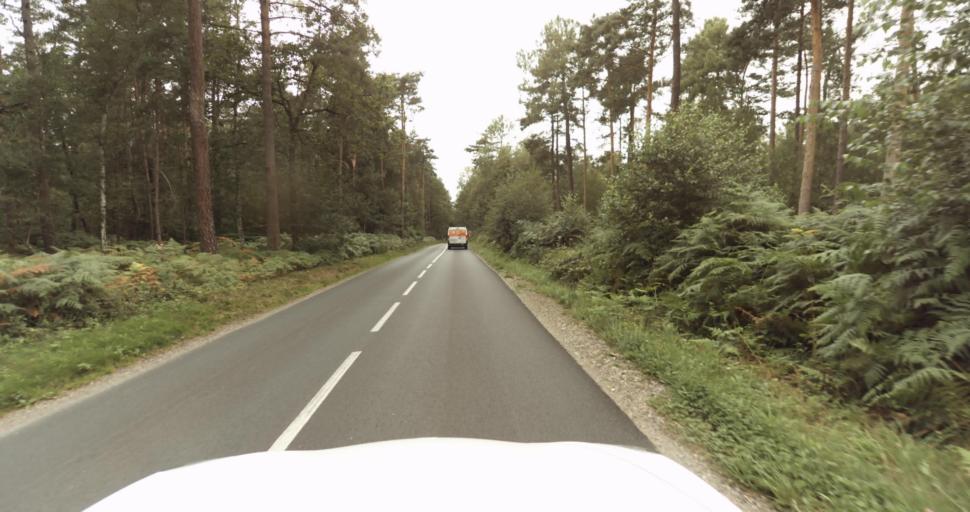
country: FR
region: Haute-Normandie
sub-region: Departement de l'Eure
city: Saint-Sebastien-de-Morsent
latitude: 48.9873
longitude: 1.0594
